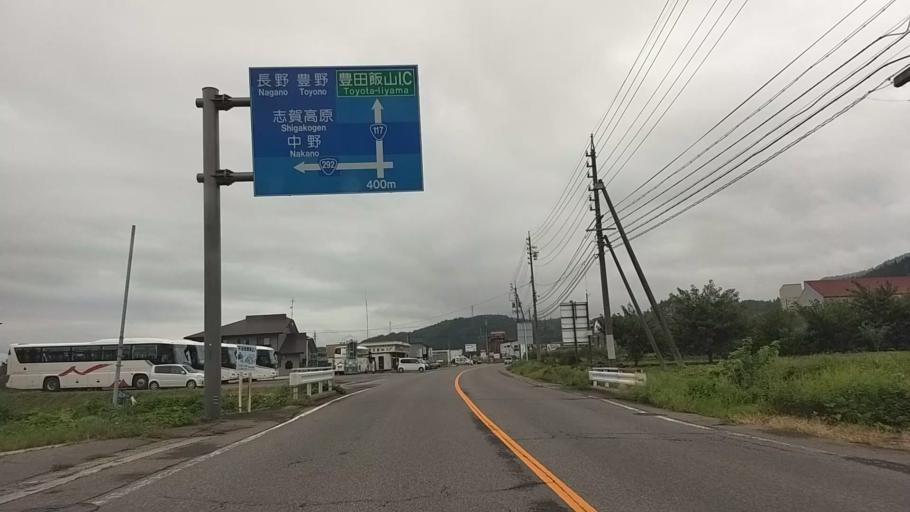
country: JP
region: Nagano
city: Iiyama
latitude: 36.8270
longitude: 138.3539
